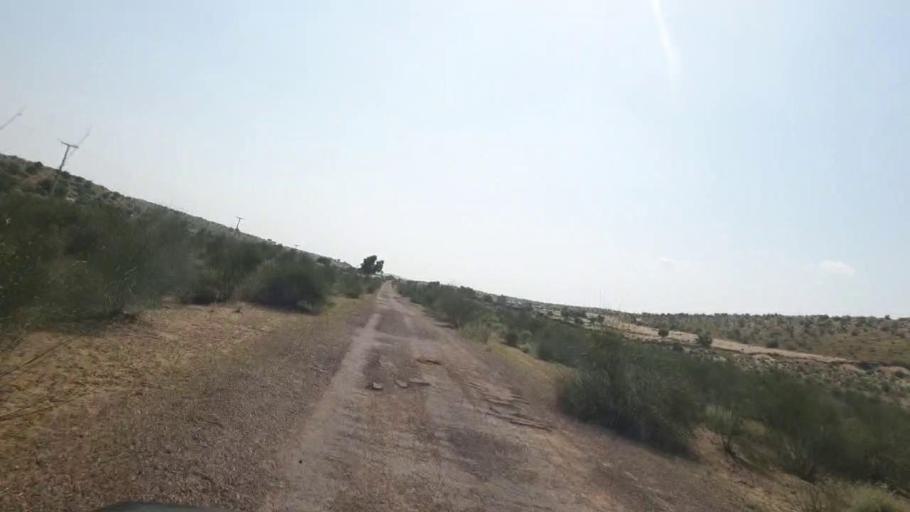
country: PK
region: Sindh
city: Chor
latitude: 25.5681
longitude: 70.2375
